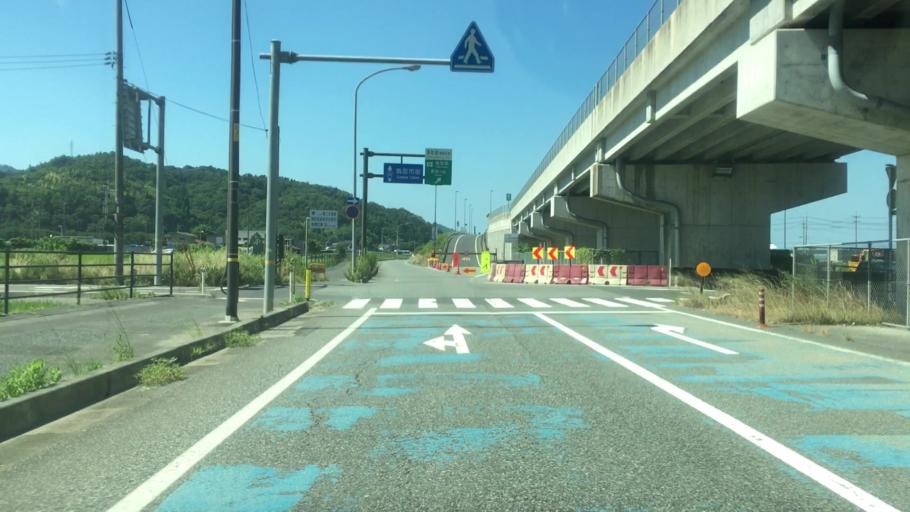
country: JP
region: Tottori
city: Tottori
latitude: 35.4302
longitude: 134.2059
